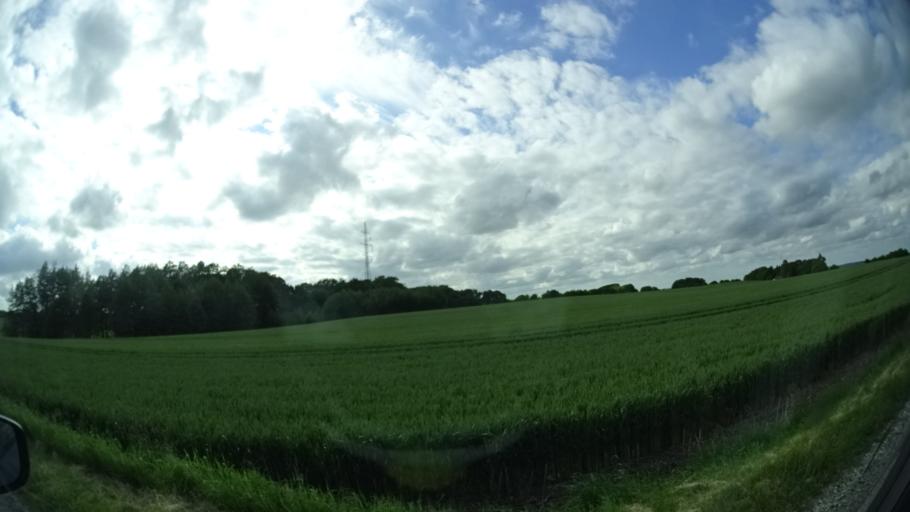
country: DK
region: Central Jutland
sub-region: Syddjurs Kommune
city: Ronde
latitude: 56.3223
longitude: 10.4328
